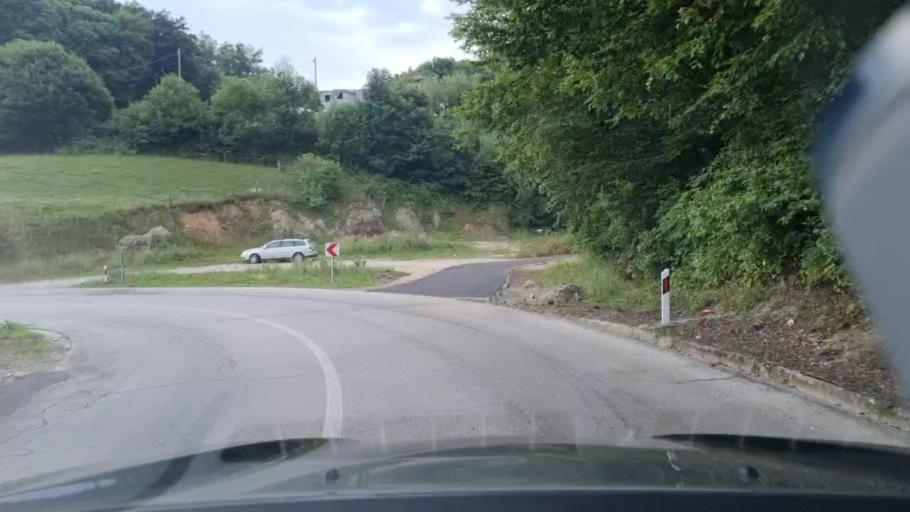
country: BA
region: Federation of Bosnia and Herzegovina
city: Podzvizd
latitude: 45.1603
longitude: 15.8997
